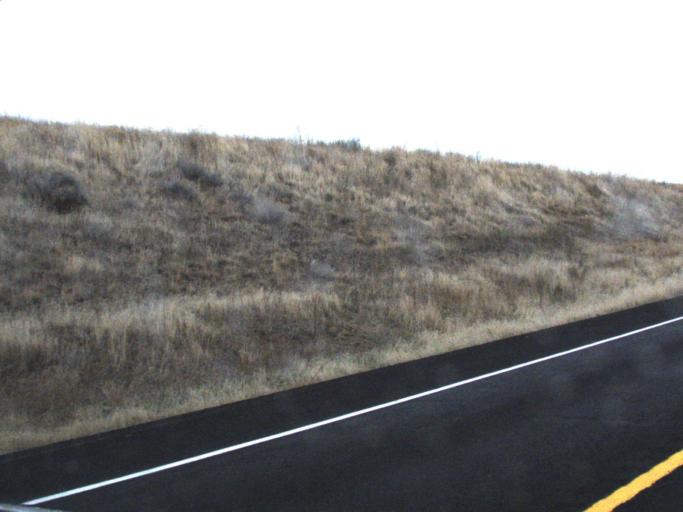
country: US
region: Washington
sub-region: Garfield County
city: Pomeroy
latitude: 46.8040
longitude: -117.7738
